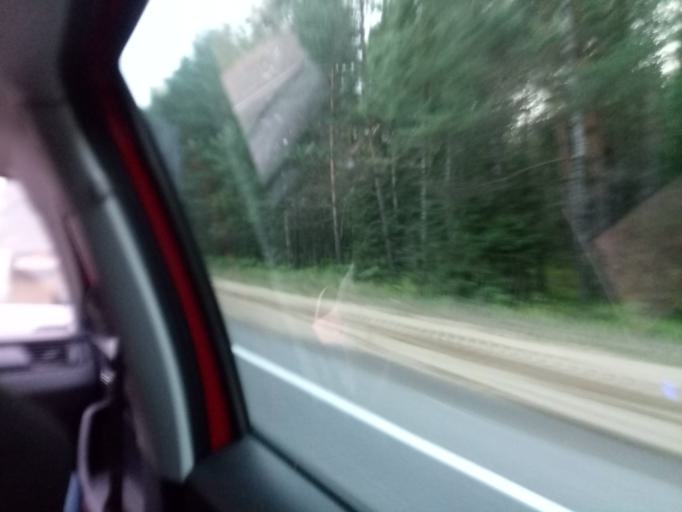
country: RU
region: Moskovskaya
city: Noginsk-9
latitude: 56.0830
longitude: 38.5767
